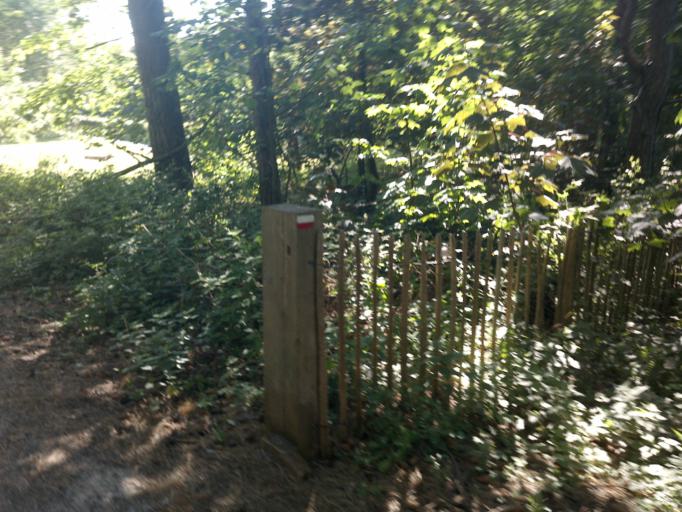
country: NL
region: South Holland
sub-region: Gemeente Noordwijkerhout
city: Noordwijkerhout
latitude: 52.2763
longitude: 4.4687
